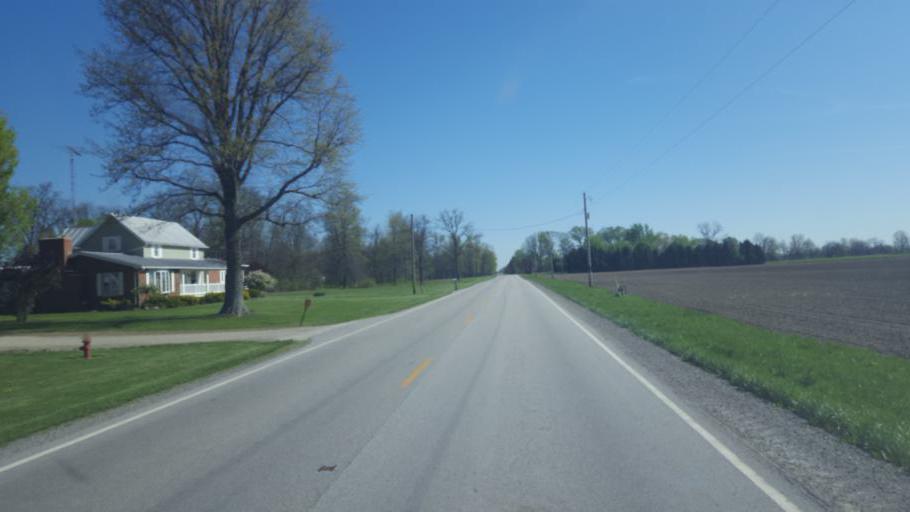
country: US
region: Ohio
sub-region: Wyandot County
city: Upper Sandusky
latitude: 40.9102
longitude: -83.2174
